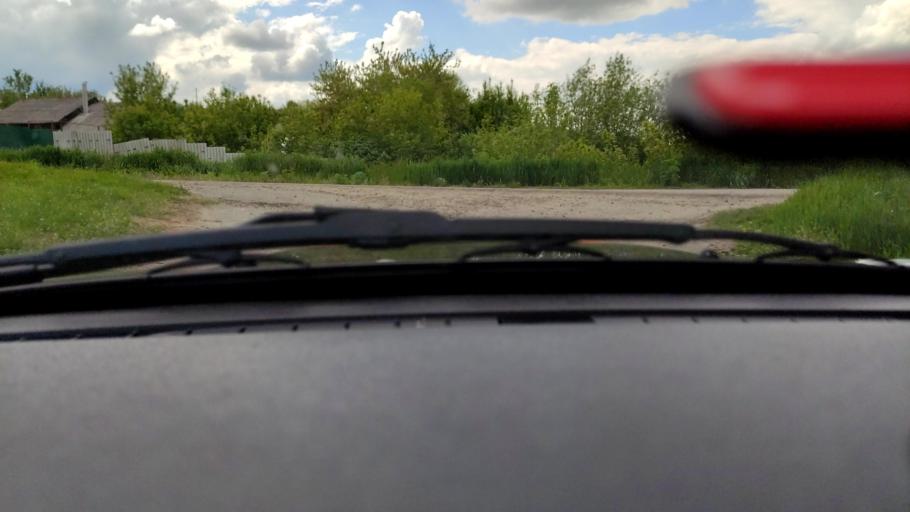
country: RU
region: Voronezj
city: Uryv-Pokrovka
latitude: 51.1064
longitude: 39.1547
